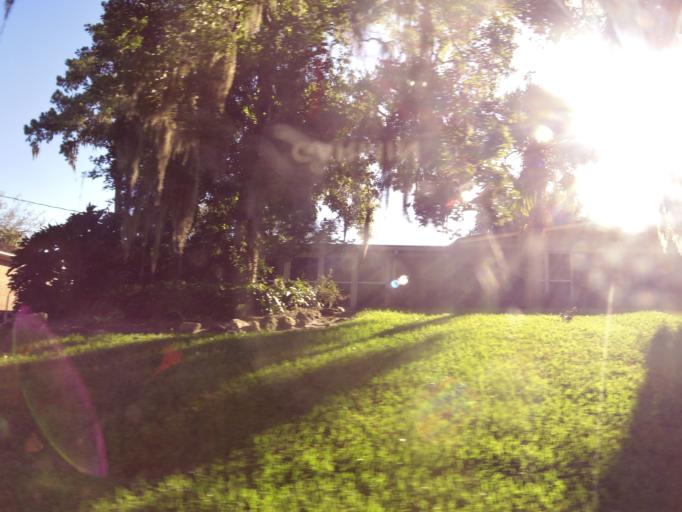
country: US
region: Florida
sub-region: Duval County
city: Jacksonville
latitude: 30.2544
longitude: -81.6316
